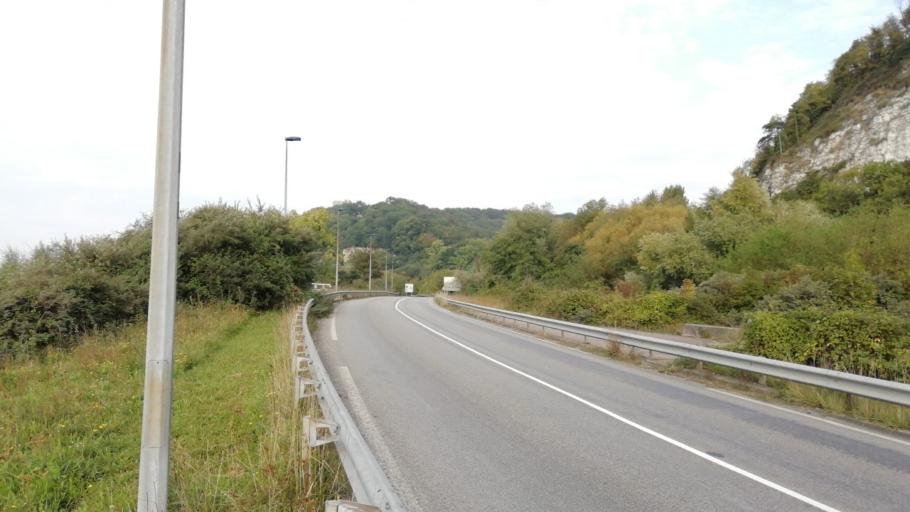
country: FR
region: Haute-Normandie
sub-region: Departement de la Seine-Maritime
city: Rogerville
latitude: 49.4956
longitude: 0.2560
